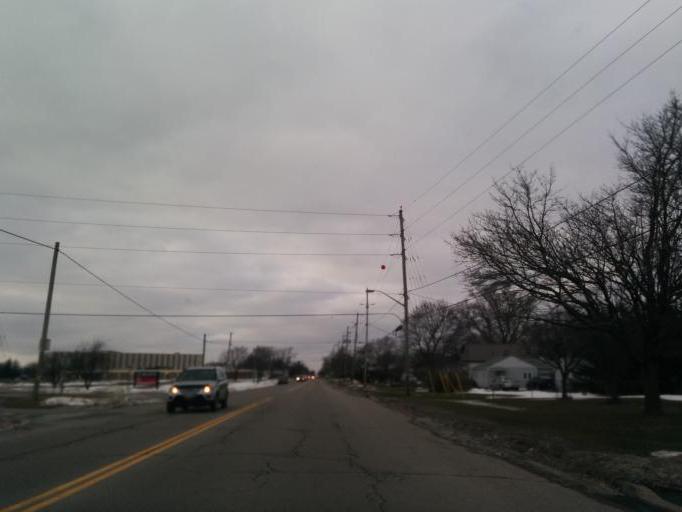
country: CA
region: Ontario
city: Ancaster
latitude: 42.9582
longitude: -80.0410
